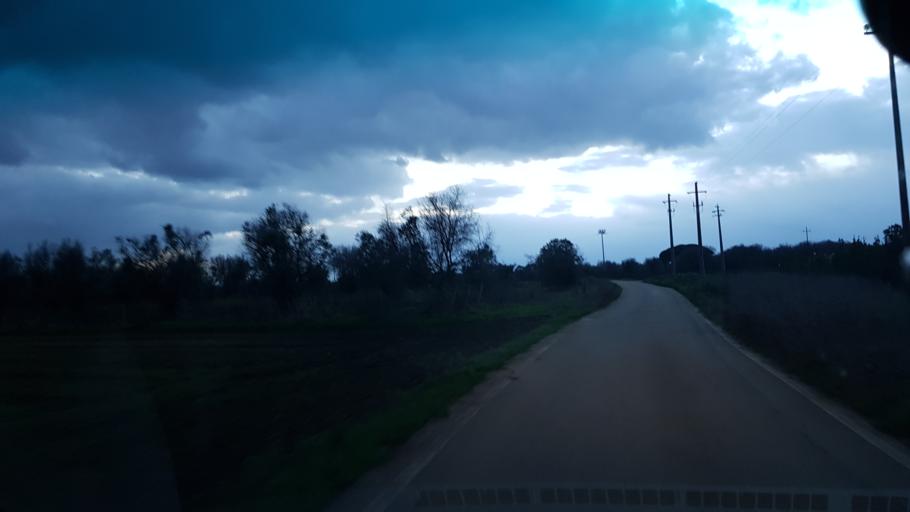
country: IT
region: Apulia
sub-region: Provincia di Brindisi
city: Torchiarolo
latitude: 40.5237
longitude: 18.0342
